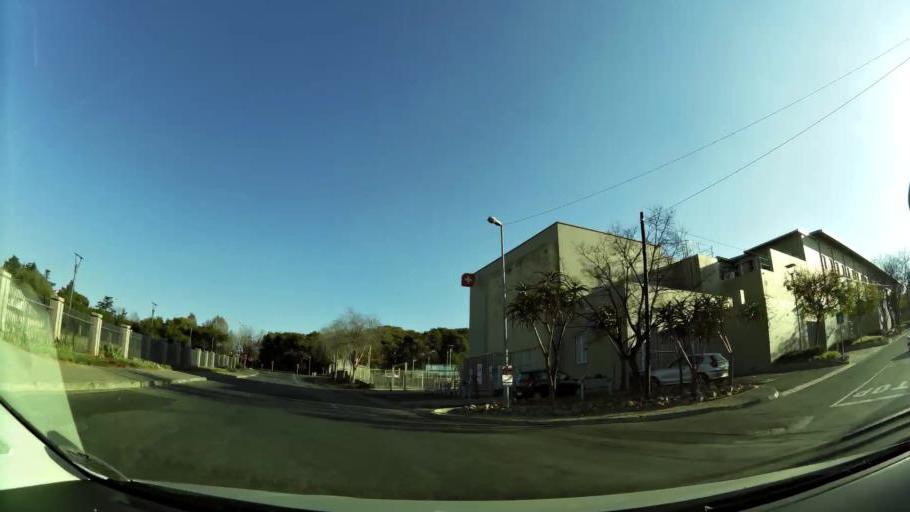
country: ZA
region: Gauteng
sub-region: City of Johannesburg Metropolitan Municipality
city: Modderfontein
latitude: -26.1002
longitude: 28.0669
